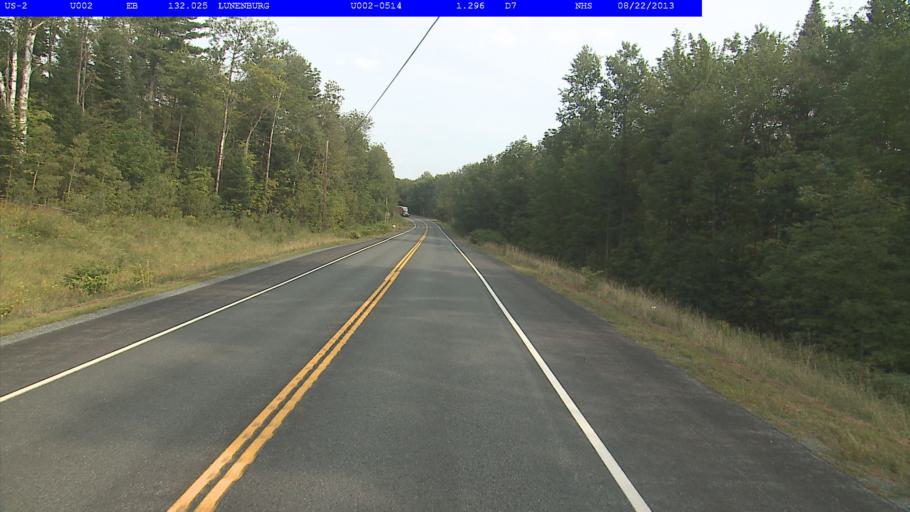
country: US
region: New Hampshire
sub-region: Grafton County
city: Littleton
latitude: 44.4665
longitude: -71.7494
